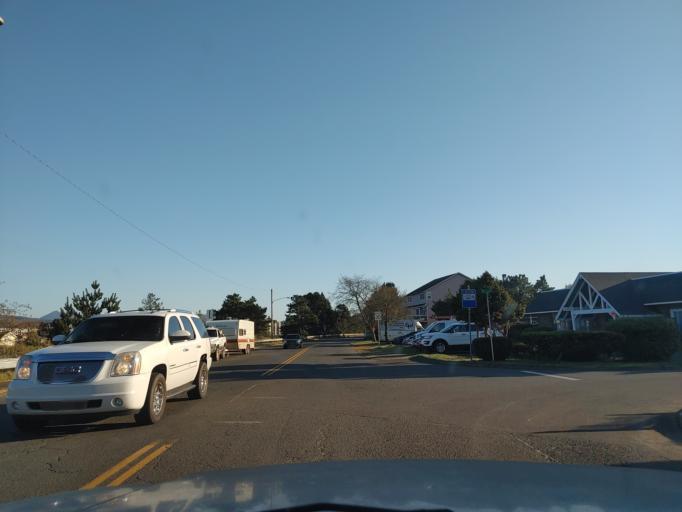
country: US
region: Oregon
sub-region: Clatsop County
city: Seaside
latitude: 45.9997
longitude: -123.9233
